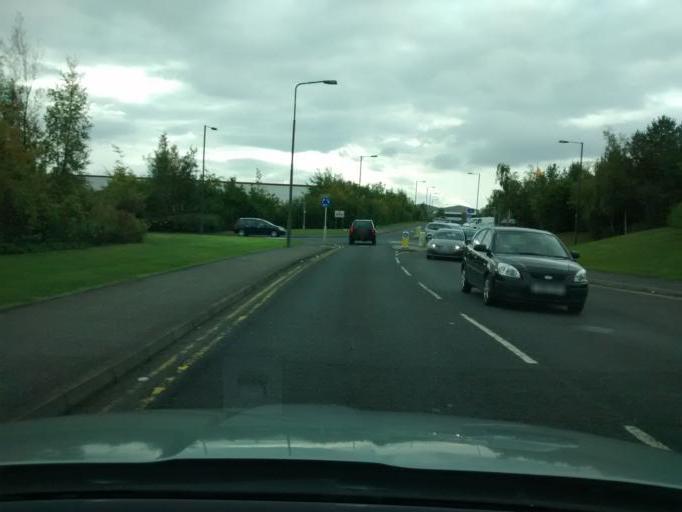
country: GB
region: Scotland
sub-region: Midlothian
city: Loanhead
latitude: 55.8815
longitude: -3.1655
